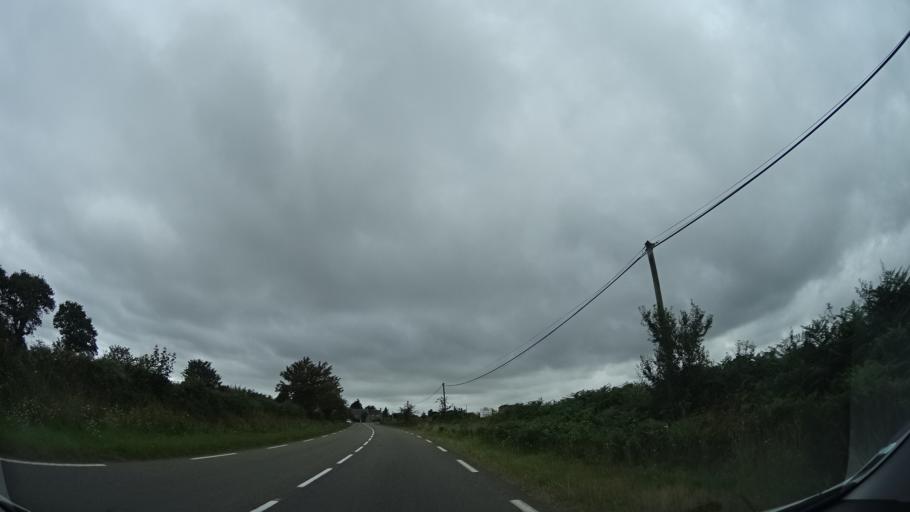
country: FR
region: Lower Normandy
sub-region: Departement de la Manche
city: La Haye-du-Puits
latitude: 49.3073
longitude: -1.5908
